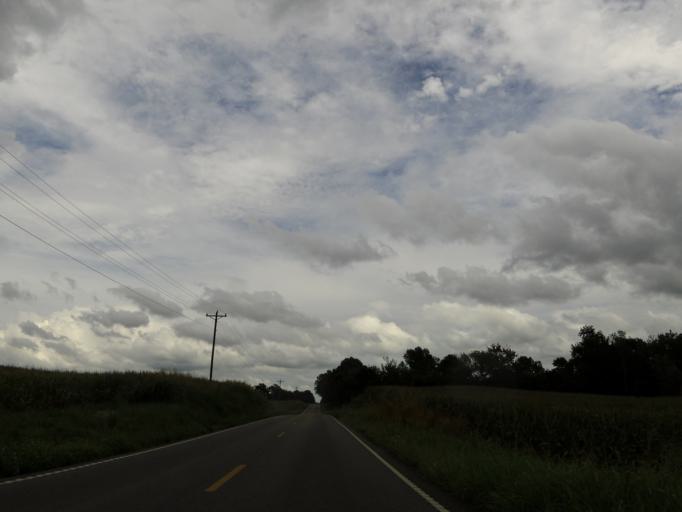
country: US
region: Kentucky
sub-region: Ballard County
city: La Center
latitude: 36.9898
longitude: -88.9699
